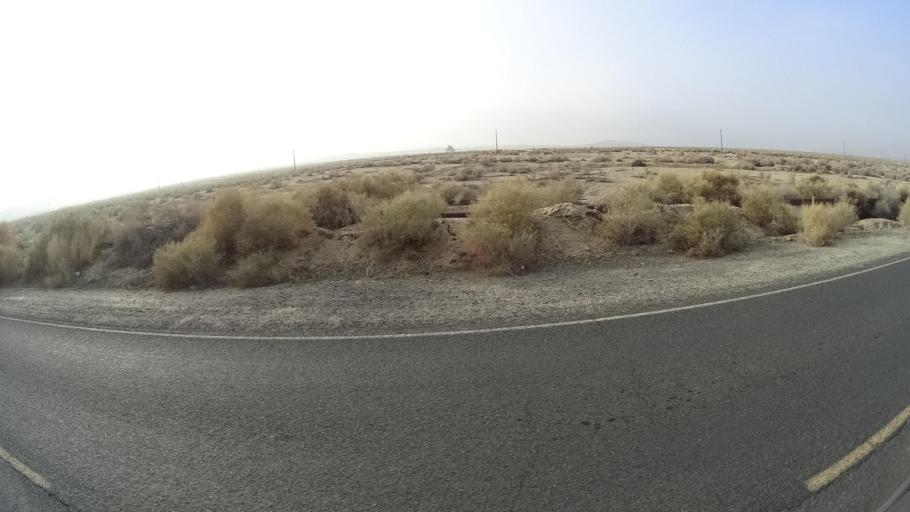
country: US
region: California
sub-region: Kern County
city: Ford City
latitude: 35.2121
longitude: -119.4455
